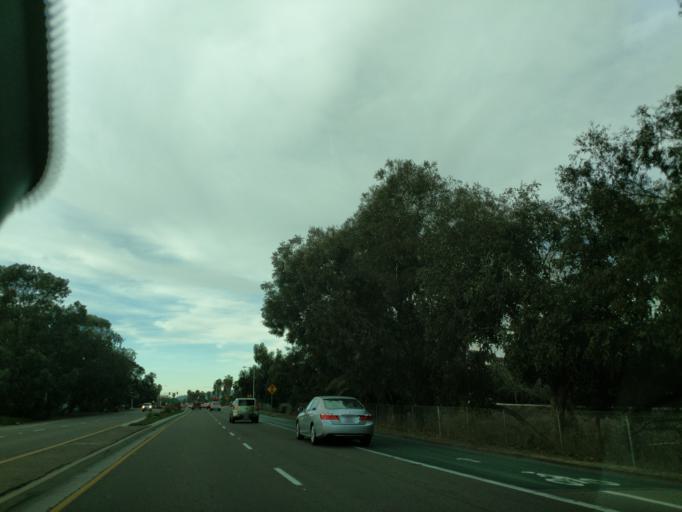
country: US
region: California
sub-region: San Diego County
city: Coronado
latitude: 32.7489
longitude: -117.2349
